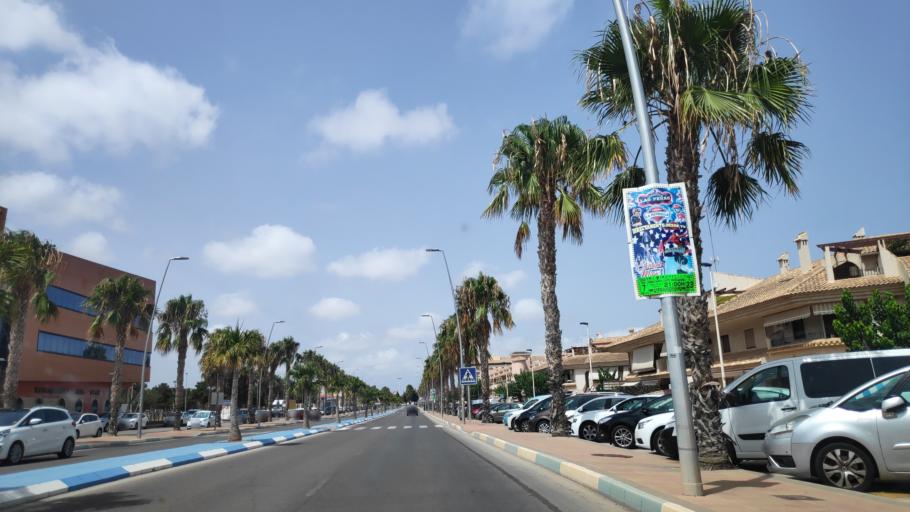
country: ES
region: Murcia
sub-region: Murcia
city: Los Alcazares
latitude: 37.7513
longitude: -0.8474
